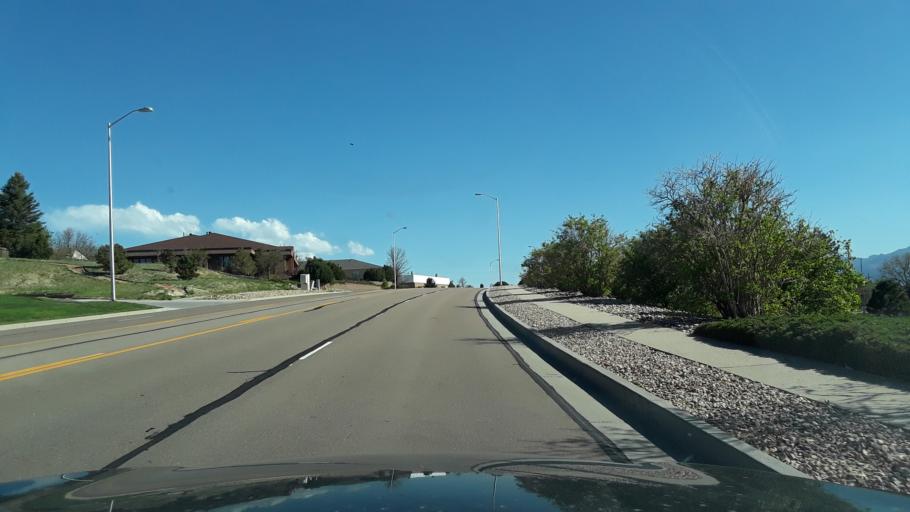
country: US
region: Colorado
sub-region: El Paso County
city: Air Force Academy
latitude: 38.9473
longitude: -104.7916
